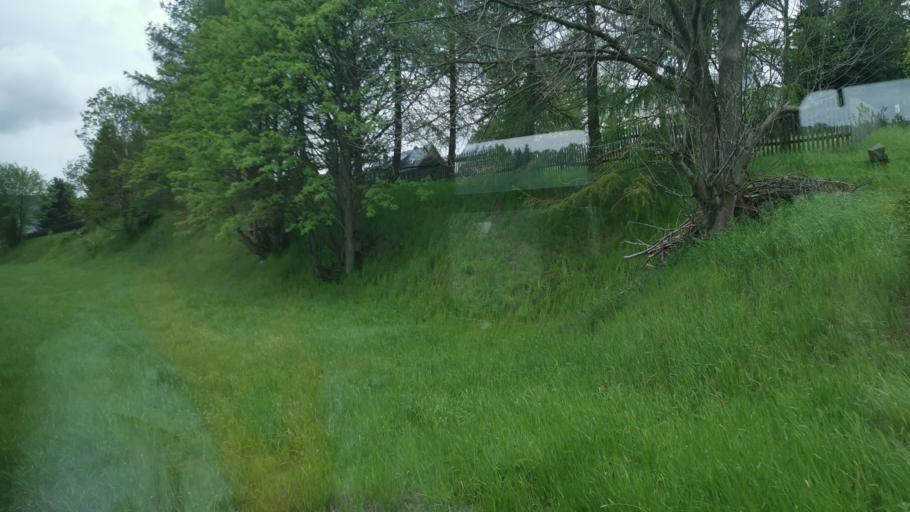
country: DE
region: Saxony
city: Kurort Oberwiesenthal
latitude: 50.4246
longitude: 12.9876
